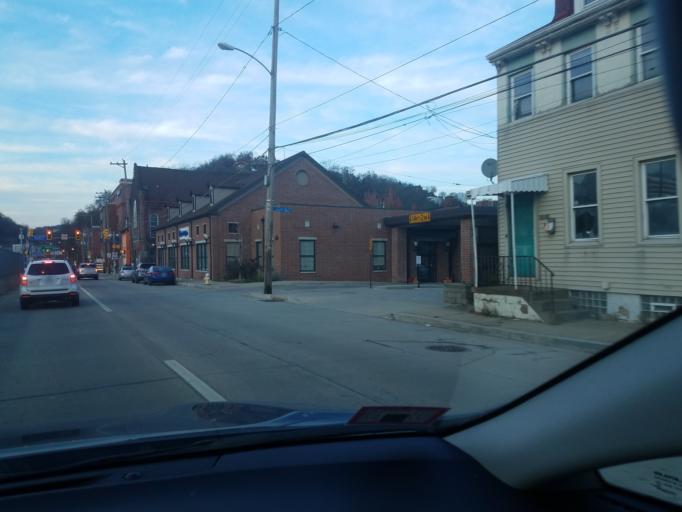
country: US
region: Pennsylvania
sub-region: Allegheny County
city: Pittsburgh
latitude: 40.4559
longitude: -79.9975
